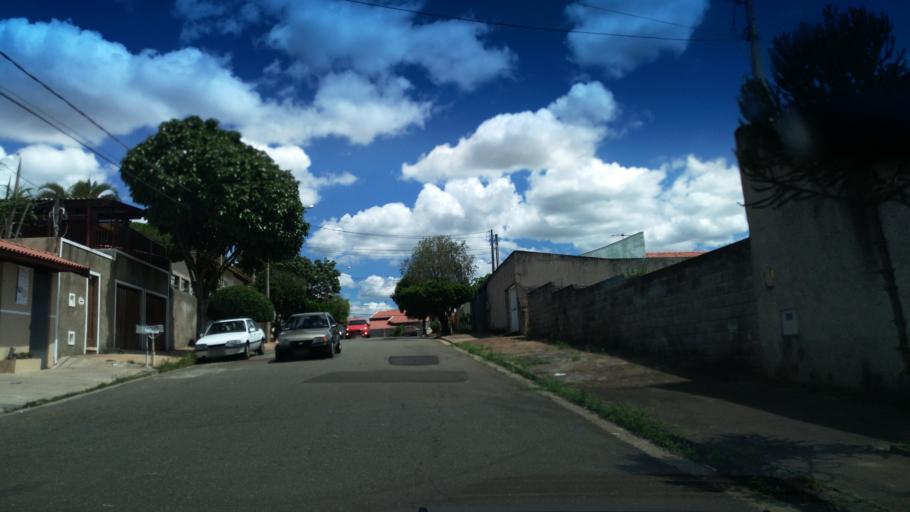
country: BR
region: Sao Paulo
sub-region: Valinhos
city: Valinhos
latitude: -22.9528
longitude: -46.9772
